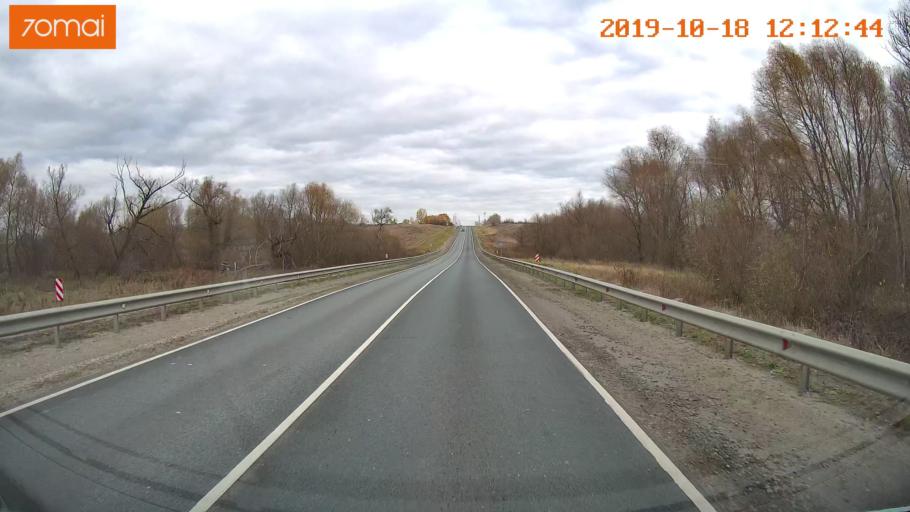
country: RU
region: Rjazan
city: Zakharovo
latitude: 54.4147
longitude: 39.3616
